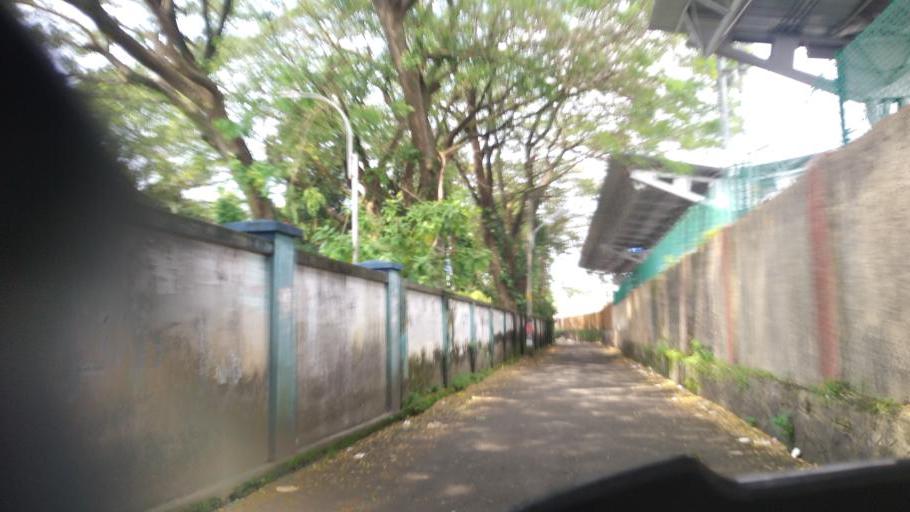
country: IN
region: Kerala
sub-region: Ernakulam
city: Cochin
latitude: 9.9942
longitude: 76.2859
